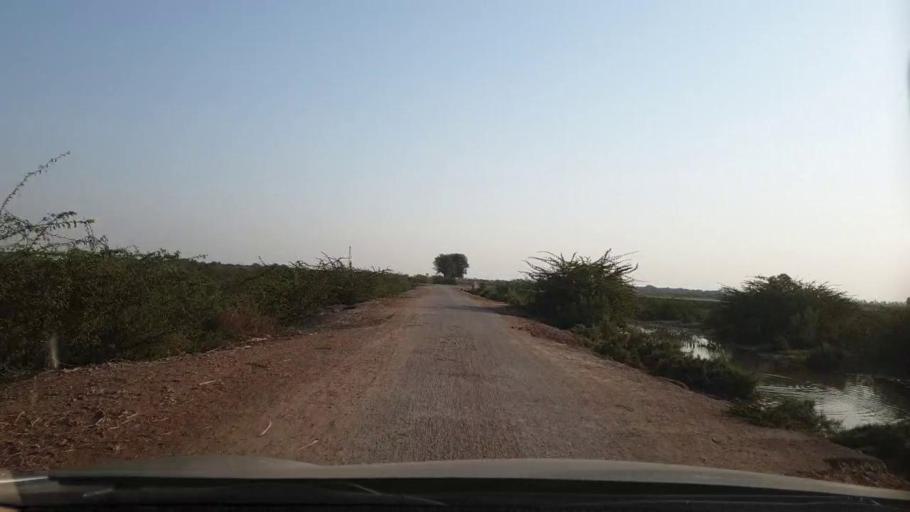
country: PK
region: Sindh
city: Berani
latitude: 25.6482
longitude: 68.8064
